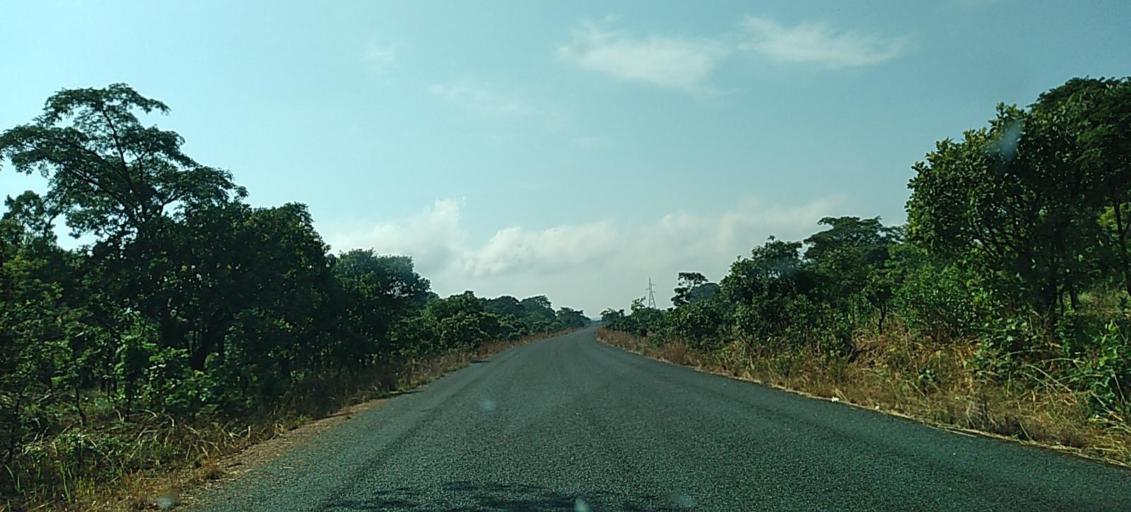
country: ZM
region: North-Western
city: Mwinilunga
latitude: -11.7375
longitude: 24.9812
